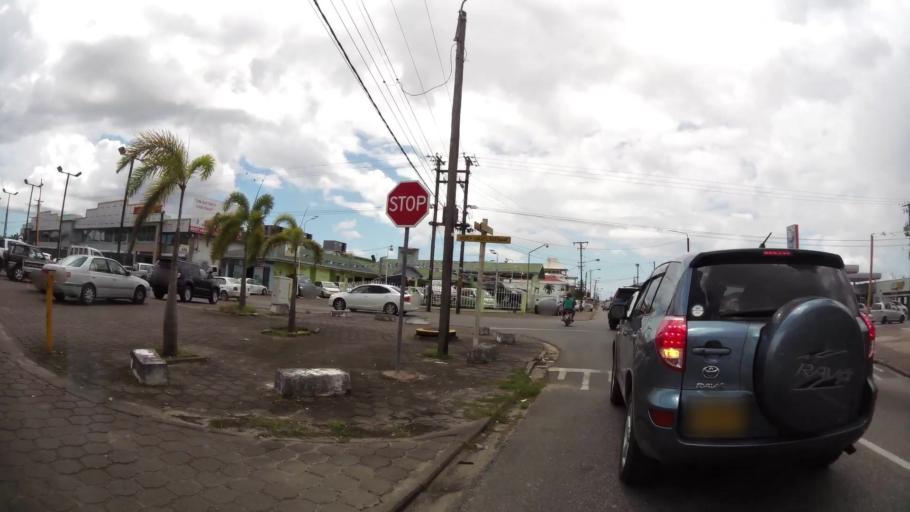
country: SR
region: Paramaribo
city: Paramaribo
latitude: 5.8539
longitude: -55.1371
